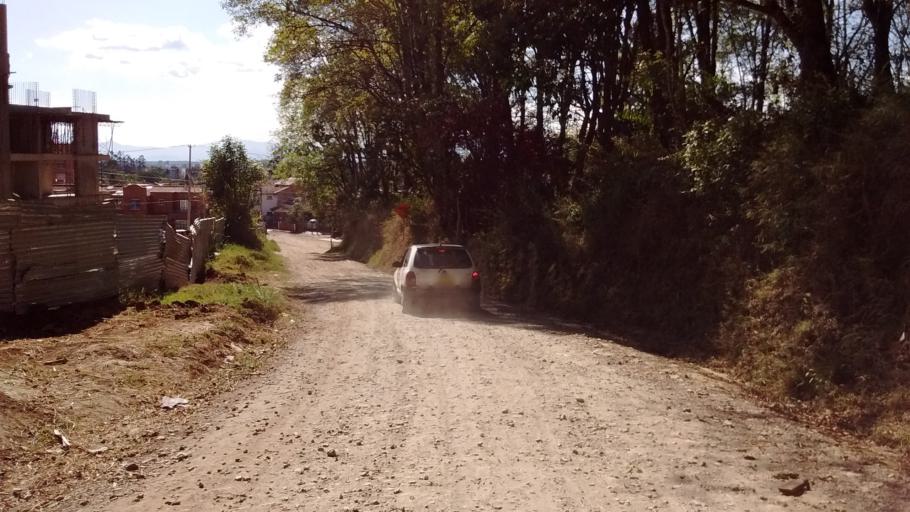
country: CO
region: Cauca
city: Popayan
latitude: 2.4662
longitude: -76.5784
